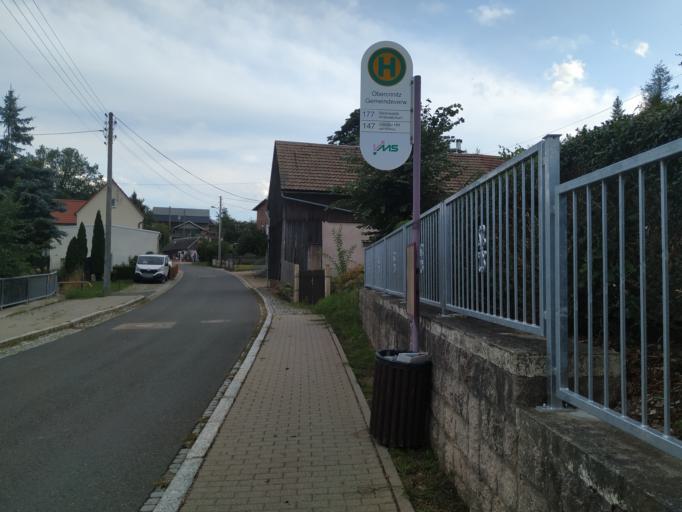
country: DE
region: Saxony
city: Stutzengrun
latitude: 50.5694
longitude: 12.4813
